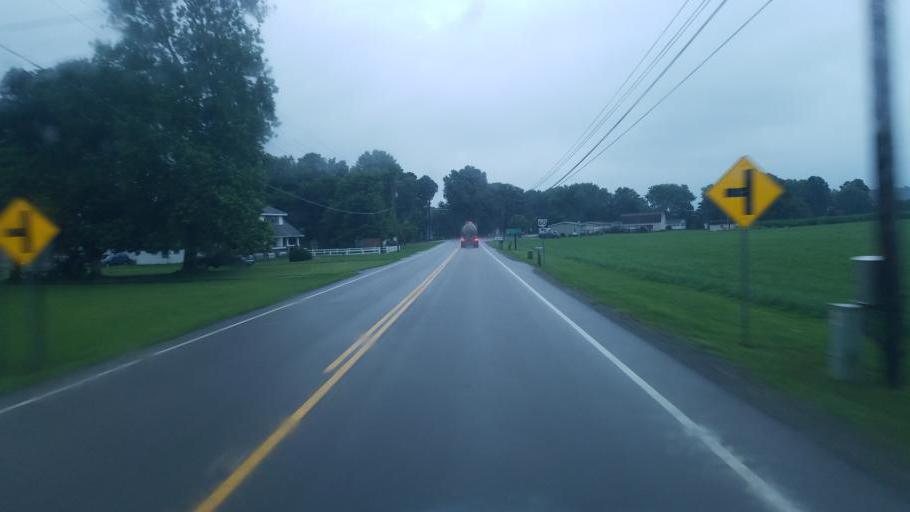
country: US
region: Ohio
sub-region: Coshocton County
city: Coshocton
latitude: 40.3361
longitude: -81.9629
